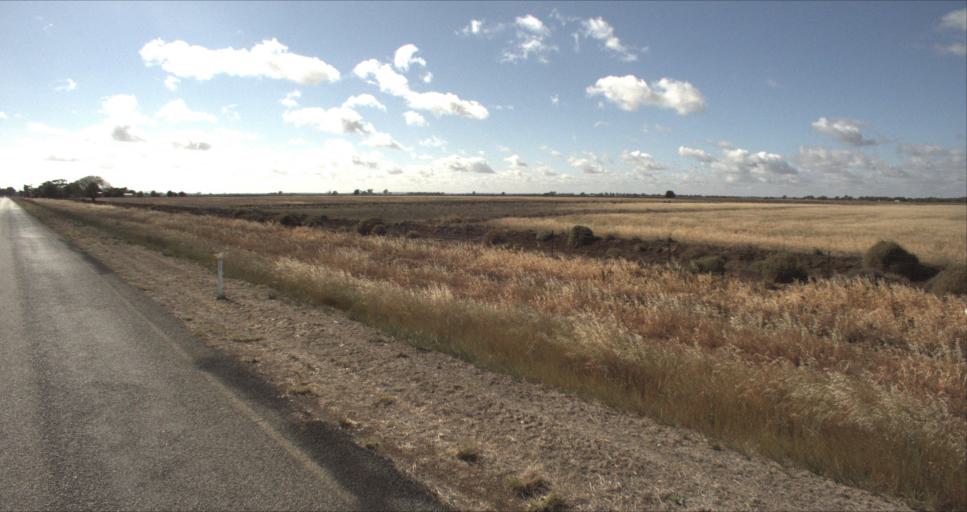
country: AU
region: New South Wales
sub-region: Leeton
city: Leeton
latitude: -34.5522
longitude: 146.3003
